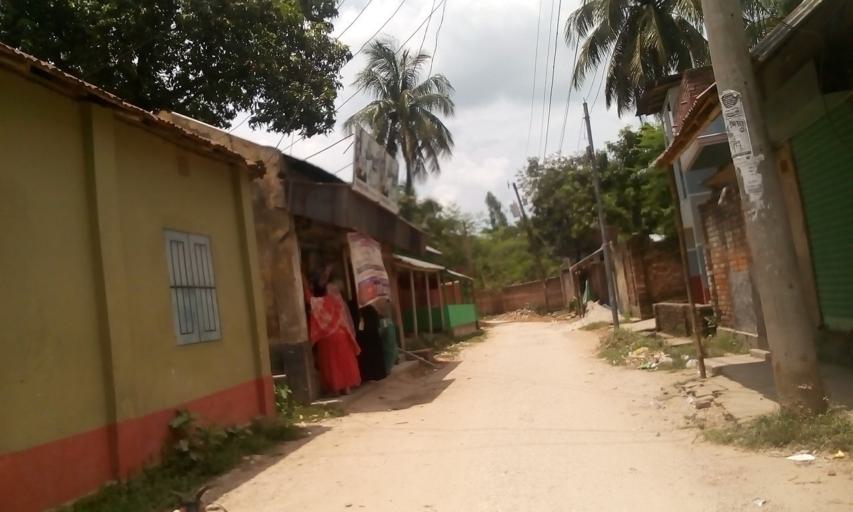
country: IN
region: West Bengal
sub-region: Dakshin Dinajpur
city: Balurghat
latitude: 25.3922
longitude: 88.9879
